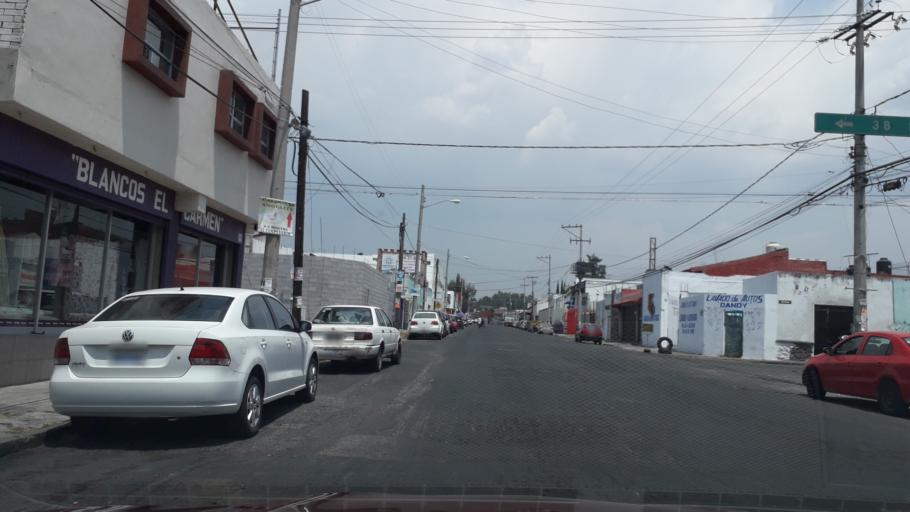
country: MX
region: Puebla
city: Puebla
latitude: 19.0453
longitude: -98.1687
